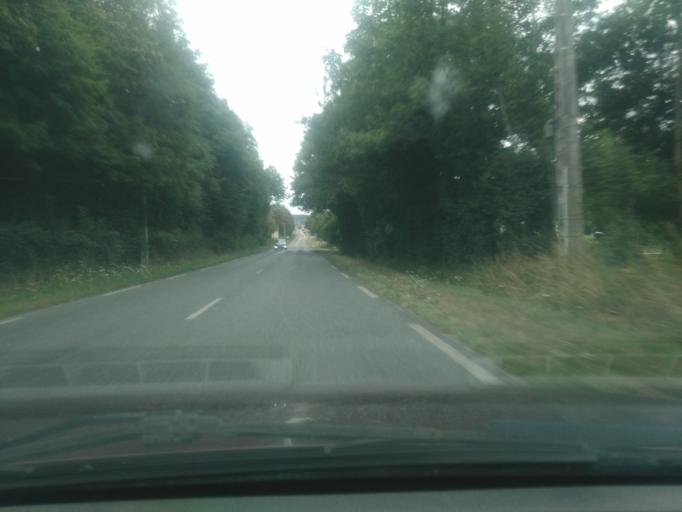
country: FR
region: Bourgogne
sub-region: Departement de la Nievre
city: Decize
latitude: 46.8149
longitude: 3.4496
